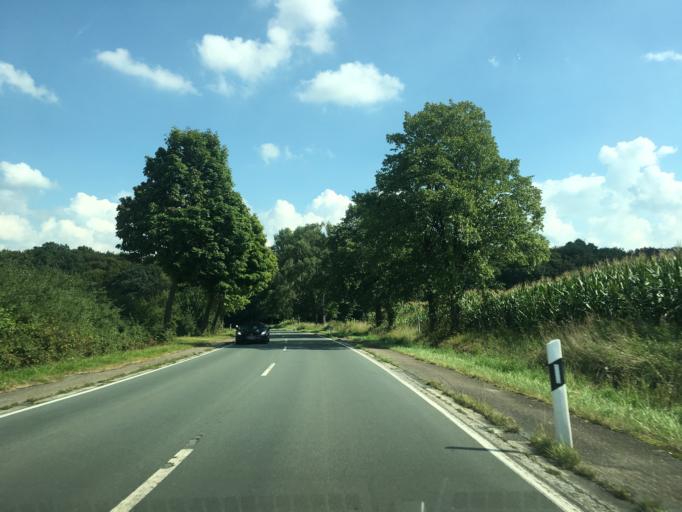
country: DE
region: North Rhine-Westphalia
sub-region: Regierungsbezirk Munster
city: Nordkirchen
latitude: 51.6791
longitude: 7.5314
